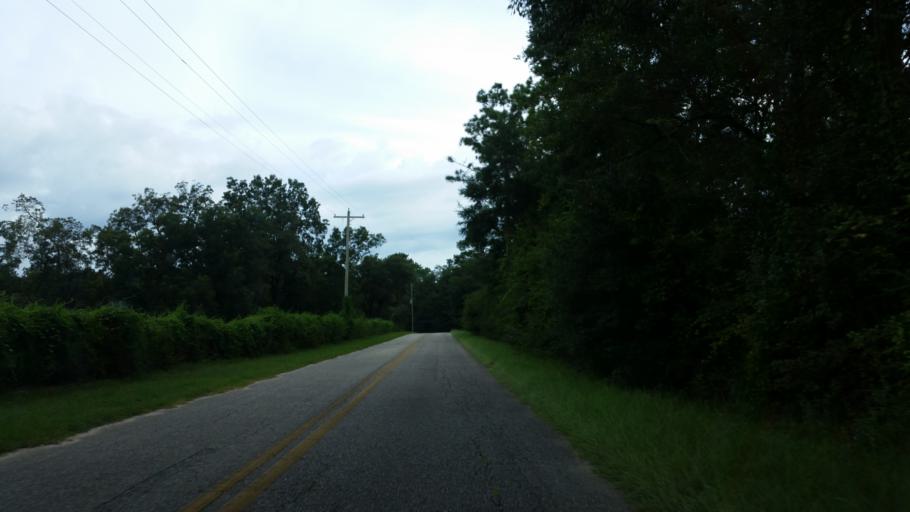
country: US
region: Florida
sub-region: Santa Rosa County
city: Point Baker
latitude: 30.7326
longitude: -86.8918
